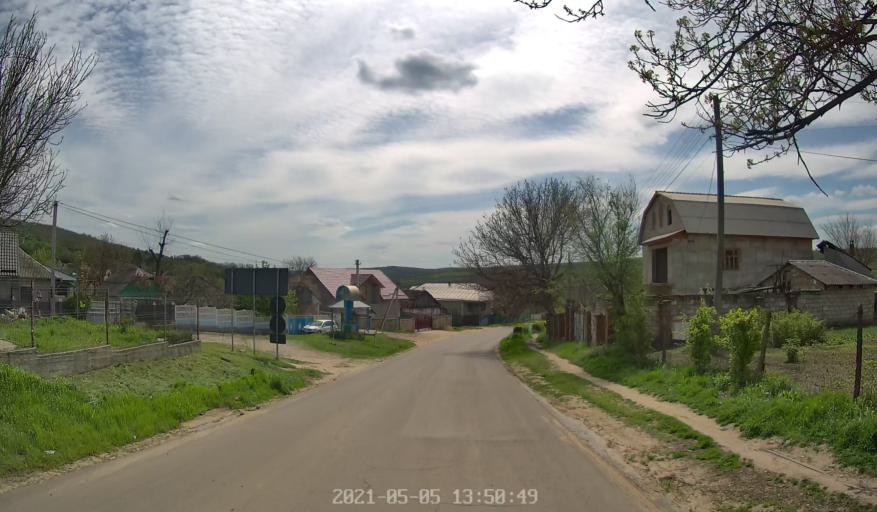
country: MD
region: Chisinau
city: Vadul lui Voda
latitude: 47.0660
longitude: 29.1323
